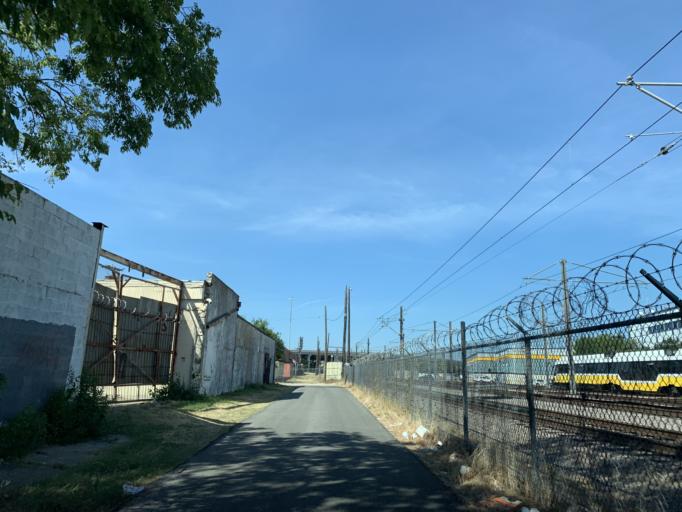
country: US
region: Texas
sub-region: Dallas County
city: Dallas
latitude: 32.7782
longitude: -96.7747
